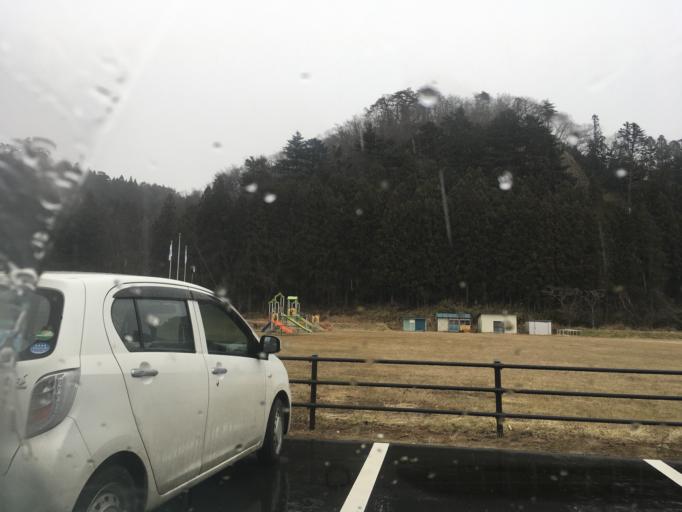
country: JP
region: Iwate
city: Ichinoseki
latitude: 38.8638
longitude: 140.9553
